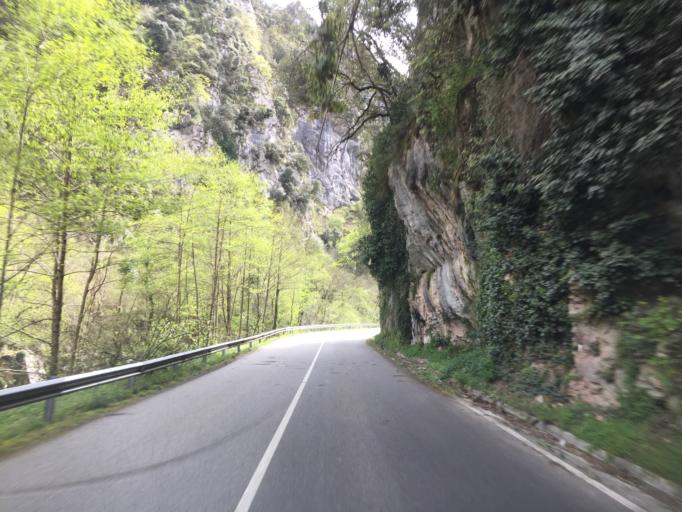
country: ES
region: Asturias
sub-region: Province of Asturias
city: Proaza
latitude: 43.2360
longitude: -6.0312
